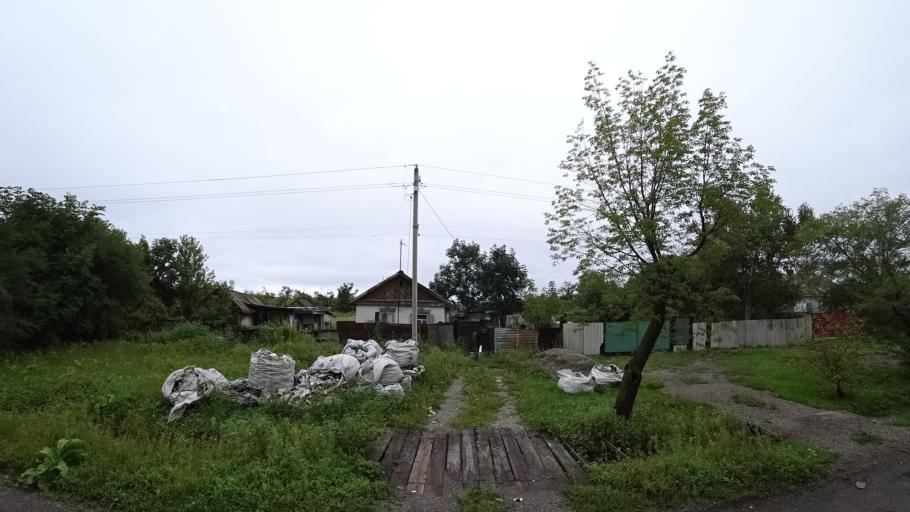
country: RU
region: Primorskiy
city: Monastyrishche
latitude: 44.1977
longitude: 132.4691
